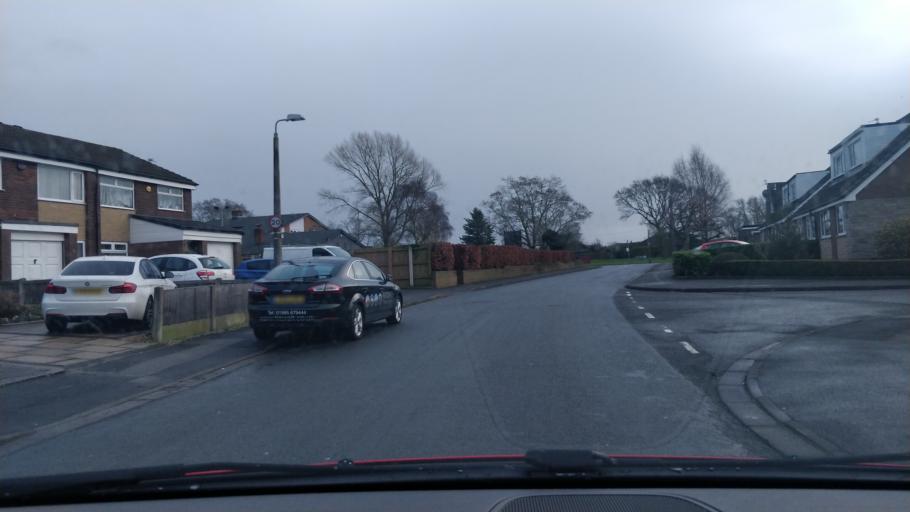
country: GB
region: England
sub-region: Lancashire
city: Preston
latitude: 53.7410
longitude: -2.7412
